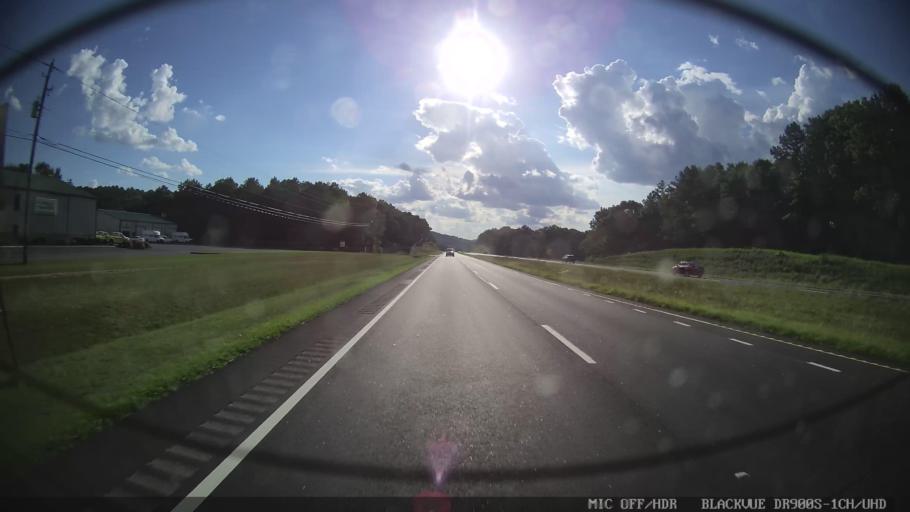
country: US
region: Georgia
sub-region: Floyd County
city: Rome
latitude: 34.2144
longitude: -85.1088
